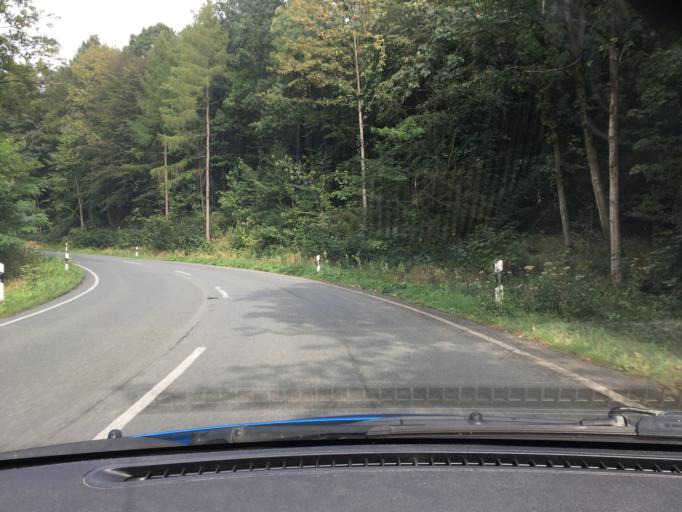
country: DE
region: Lower Saxony
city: Barsinghausen
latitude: 52.2596
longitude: 9.4658
